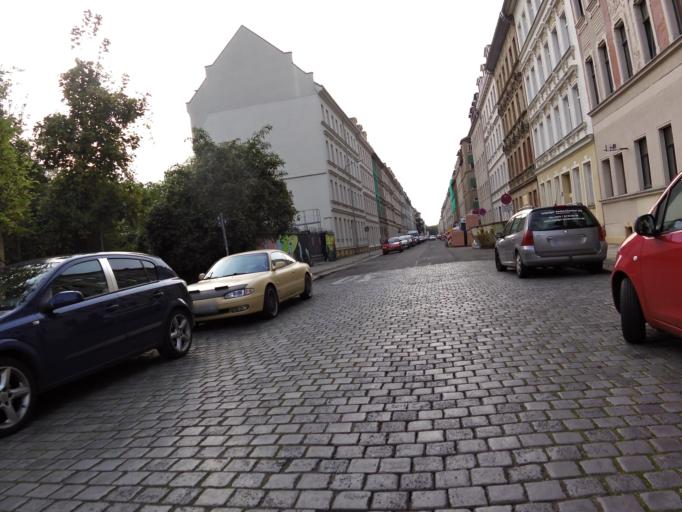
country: DE
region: Saxony
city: Leipzig
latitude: 51.3323
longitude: 12.4165
